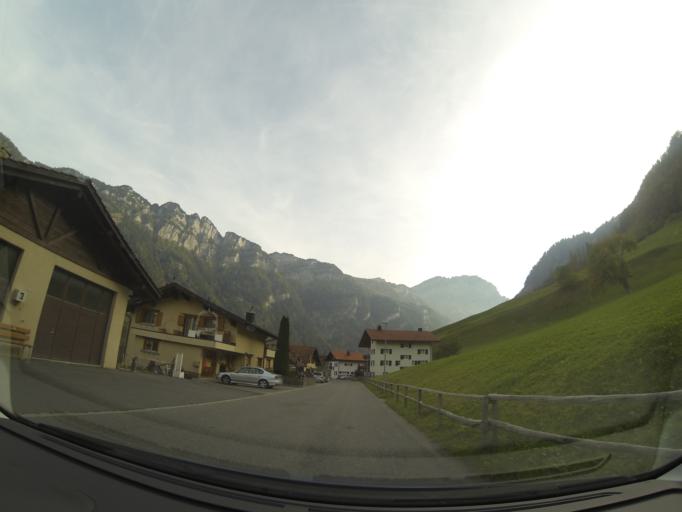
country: CH
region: Saint Gallen
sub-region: Wahlkreis Sarganserland
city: Bad Ragaz
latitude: 46.9544
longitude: 9.4766
